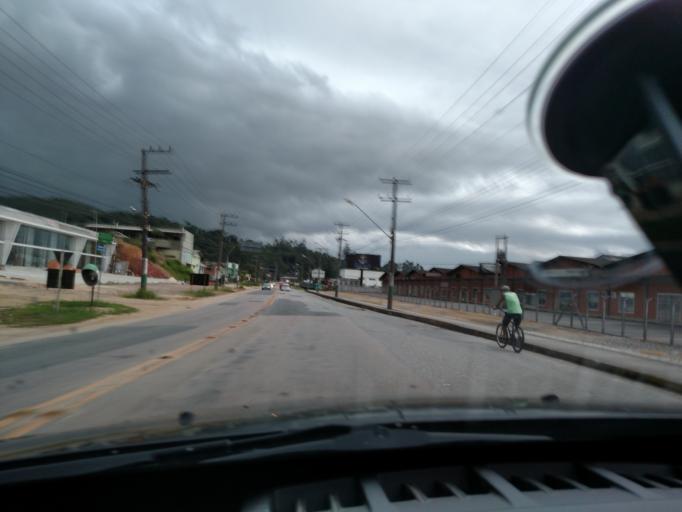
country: BR
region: Santa Catarina
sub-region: Brusque
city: Brusque
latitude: -27.0694
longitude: -48.8966
